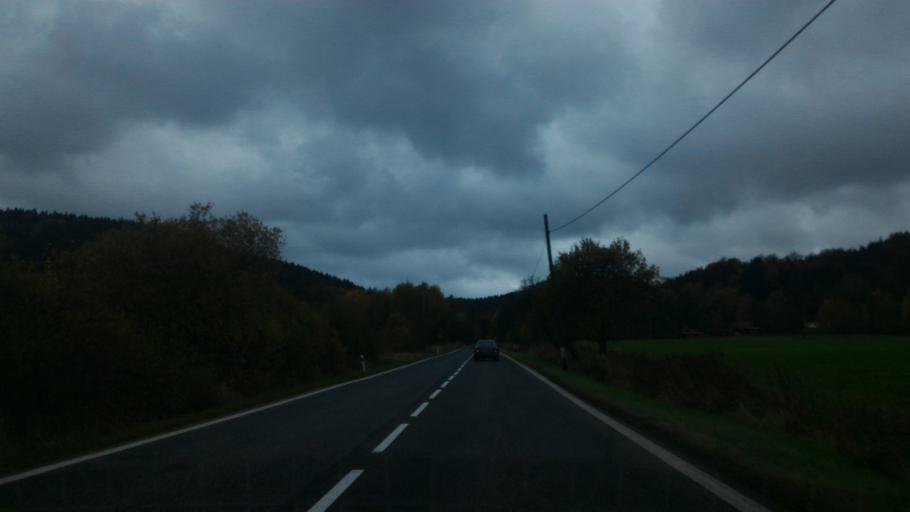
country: CZ
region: Ustecky
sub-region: Okres Decin
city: Chribska
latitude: 50.8556
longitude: 14.4770
